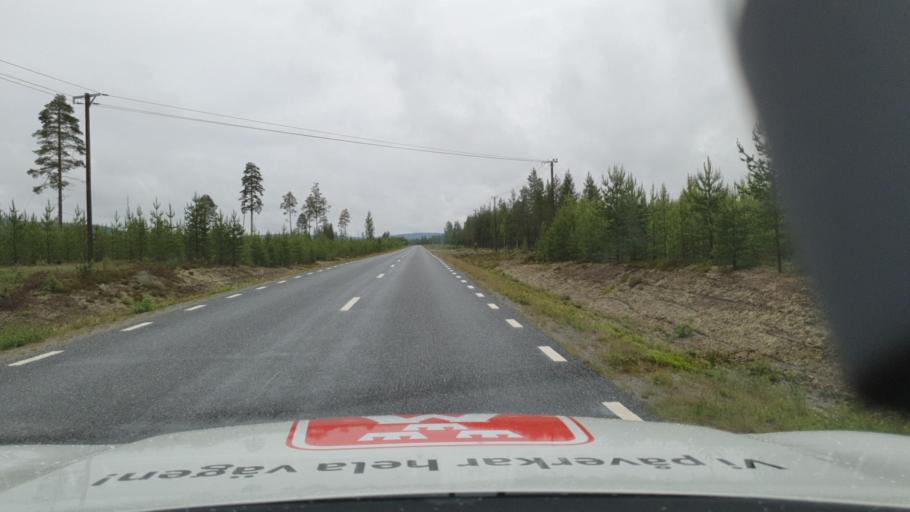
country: SE
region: Vaesterbotten
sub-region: Asele Kommun
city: Asele
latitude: 63.9513
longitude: 17.2734
